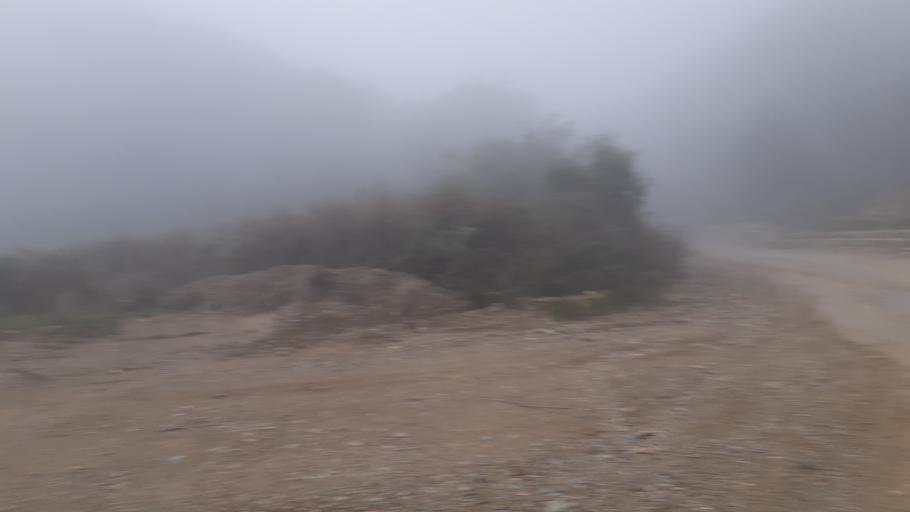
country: IT
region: Sardinia
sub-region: Provincia di Carbonia-Iglesias
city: Fluminimaggiore
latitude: 39.3994
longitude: 8.5578
